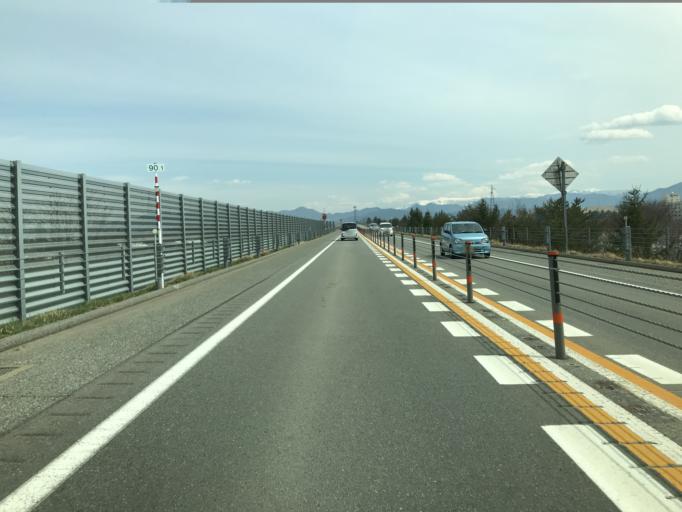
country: JP
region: Yamagata
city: Takahata
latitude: 37.9818
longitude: 140.1481
